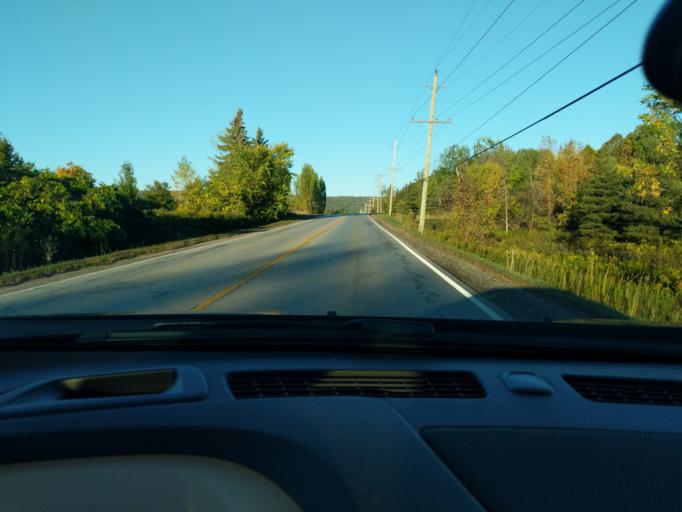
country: CA
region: Ontario
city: Collingwood
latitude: 44.4987
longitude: -80.2588
